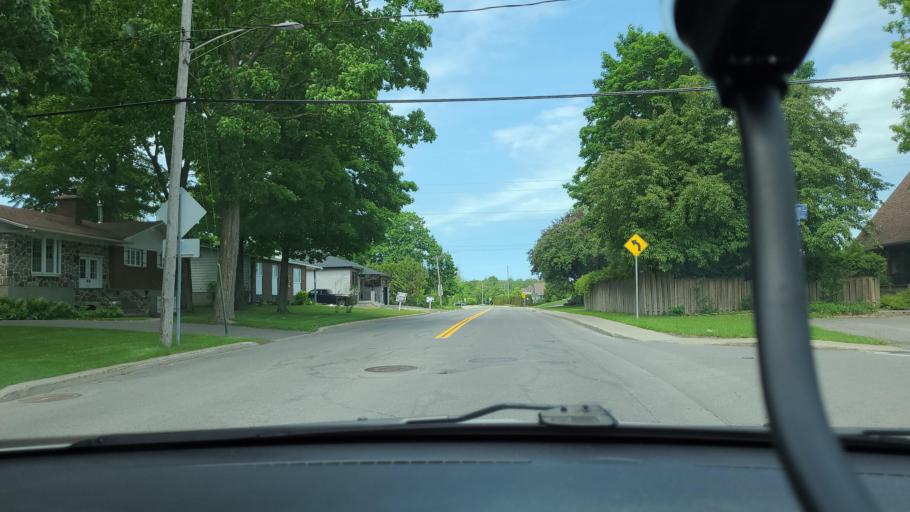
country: CA
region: Quebec
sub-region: Lanaudiere
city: Crabtree
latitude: 45.9690
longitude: -73.4803
